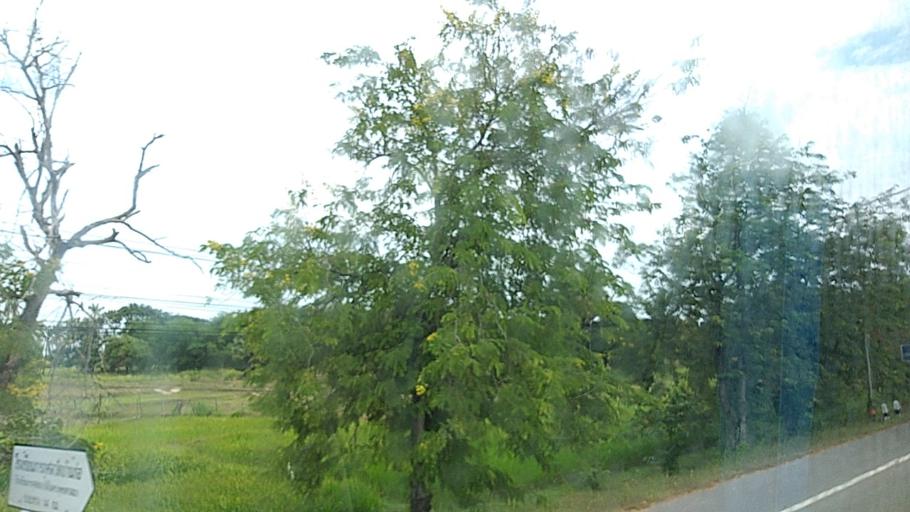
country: TH
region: Roi Et
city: Changhan
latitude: 16.1117
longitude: 103.5040
